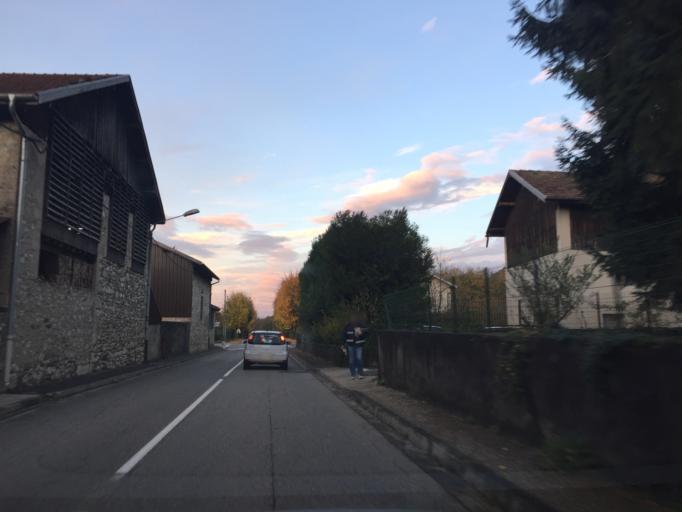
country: FR
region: Rhone-Alpes
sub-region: Departement de l'Isere
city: Saint-Sauveur
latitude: 45.1478
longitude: 5.3756
